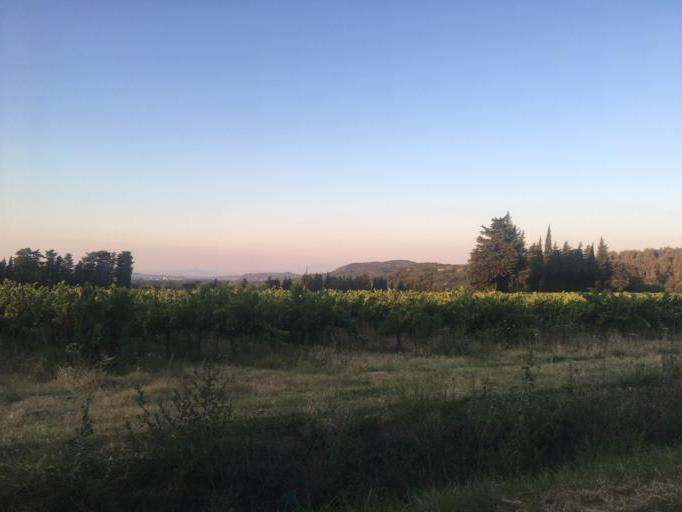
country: FR
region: Languedoc-Roussillon
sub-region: Departement du Gard
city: Saze
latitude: 43.9397
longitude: 4.6891
